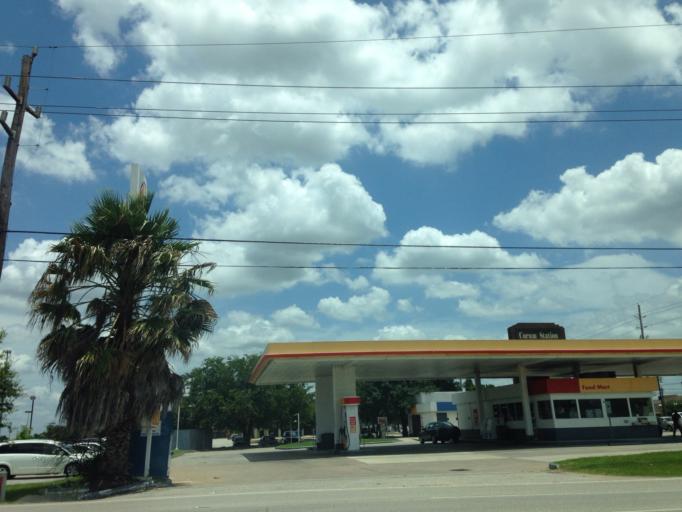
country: US
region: Texas
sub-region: Harris County
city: Spring
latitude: 30.0410
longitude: -95.4890
